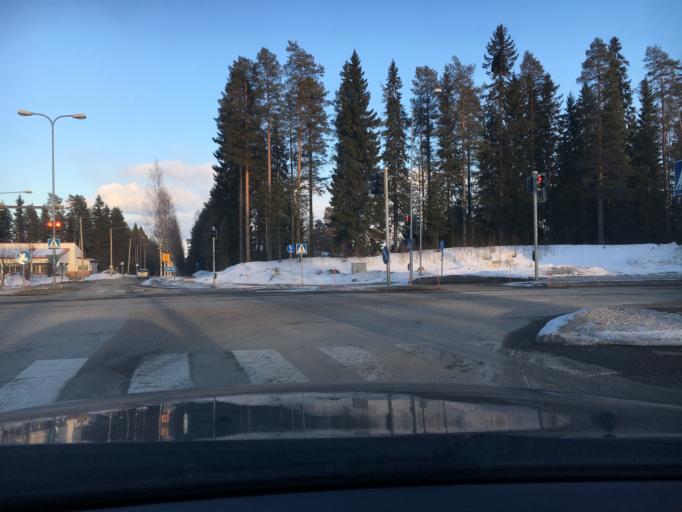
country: FI
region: Kainuu
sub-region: Kajaani
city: Kajaani
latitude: 64.2376
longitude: 27.7484
